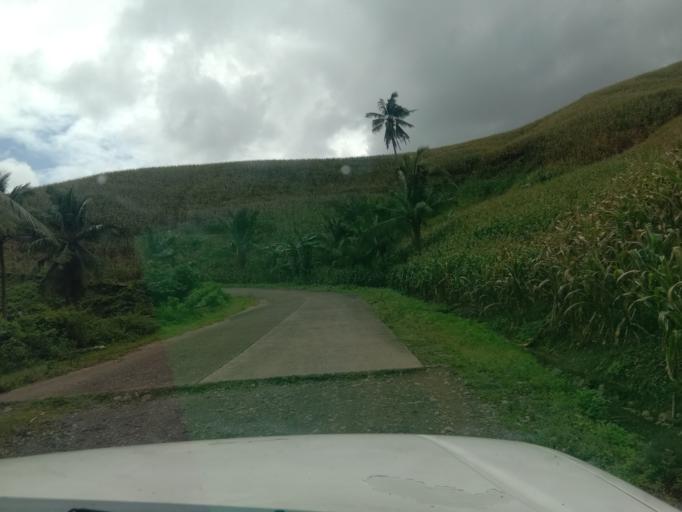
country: PH
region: Western Visayas
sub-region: Province of Capiz
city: Lantangan
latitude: 11.3551
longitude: 122.9167
